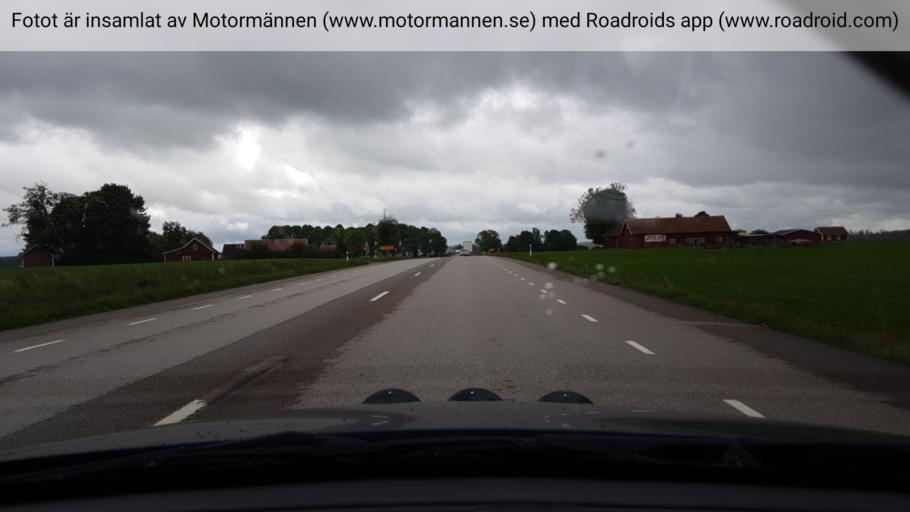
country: SE
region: Vaestra Goetaland
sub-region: Skara Kommun
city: Skara
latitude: 58.4287
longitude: 13.4693
